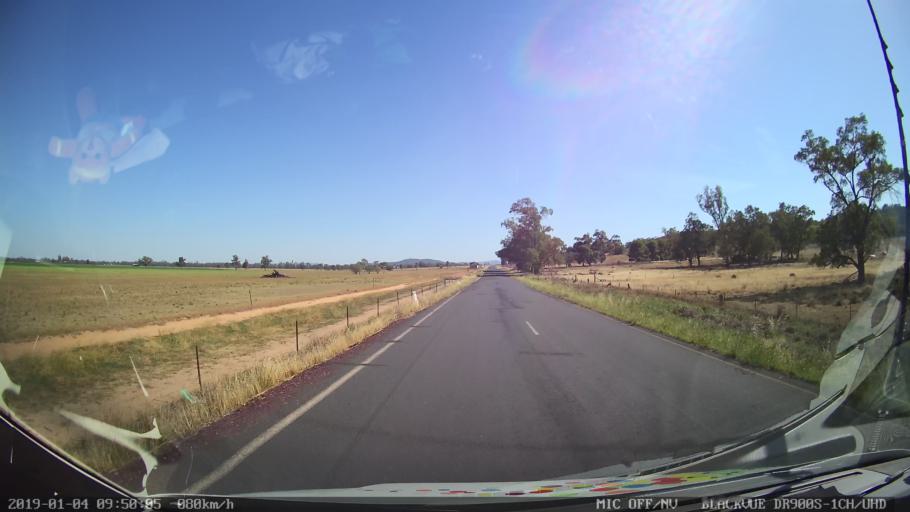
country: AU
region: New South Wales
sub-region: Cabonne
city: Canowindra
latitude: -33.5882
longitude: 148.4148
